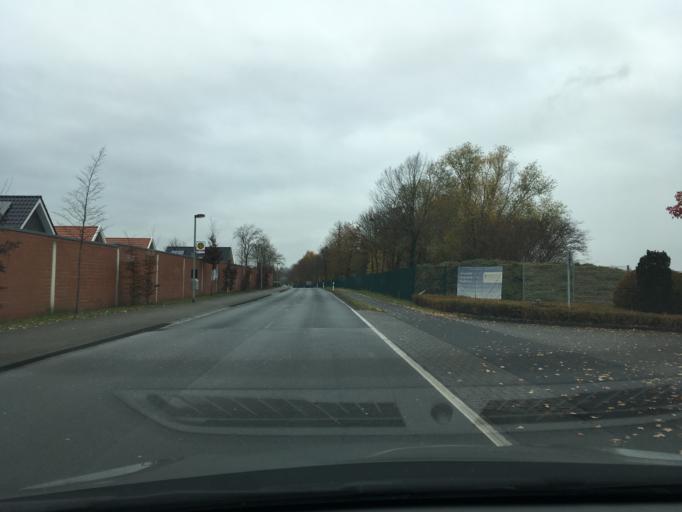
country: DE
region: North Rhine-Westphalia
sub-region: Regierungsbezirk Munster
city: Ahaus
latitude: 52.0699
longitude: 6.9837
